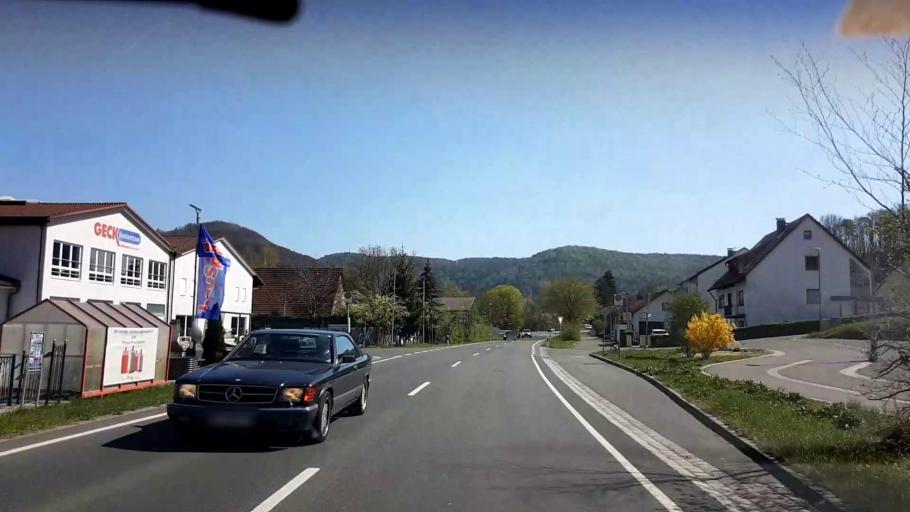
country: DE
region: Bavaria
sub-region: Upper Franconia
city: Ebermannstadt
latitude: 49.7990
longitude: 11.1978
